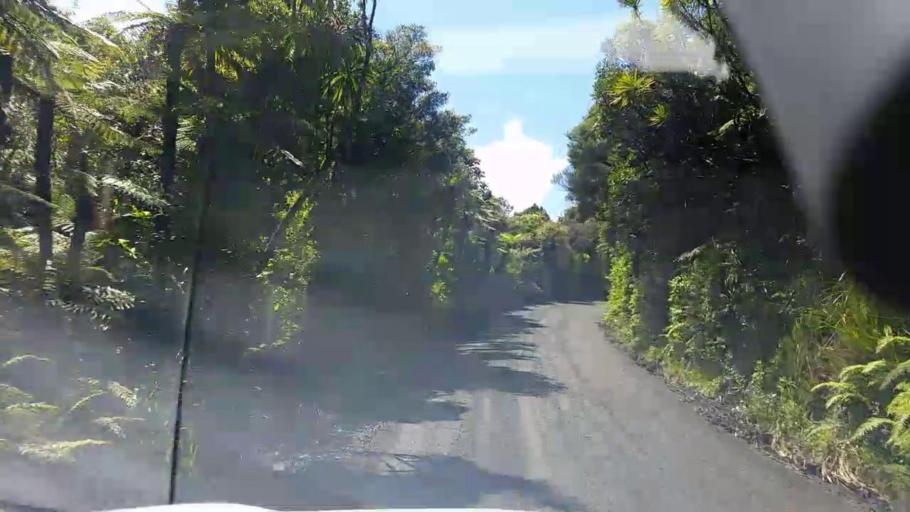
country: NZ
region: Auckland
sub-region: Auckland
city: Titirangi
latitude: -36.9416
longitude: 174.5238
